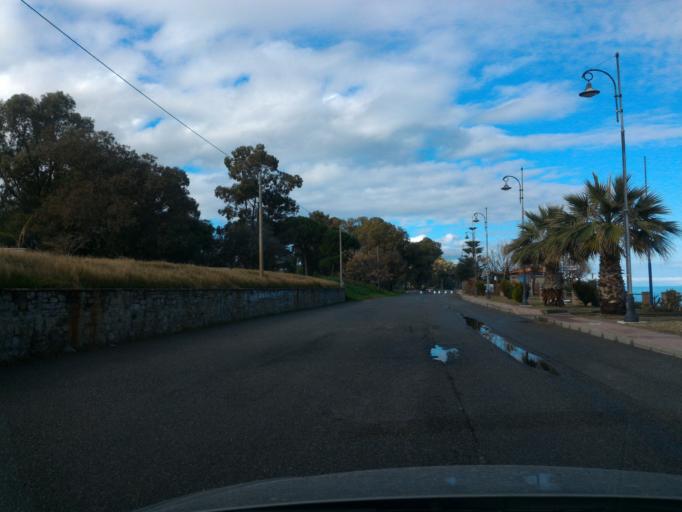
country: IT
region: Calabria
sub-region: Provincia di Crotone
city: Torretta
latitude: 39.4554
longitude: 17.0376
